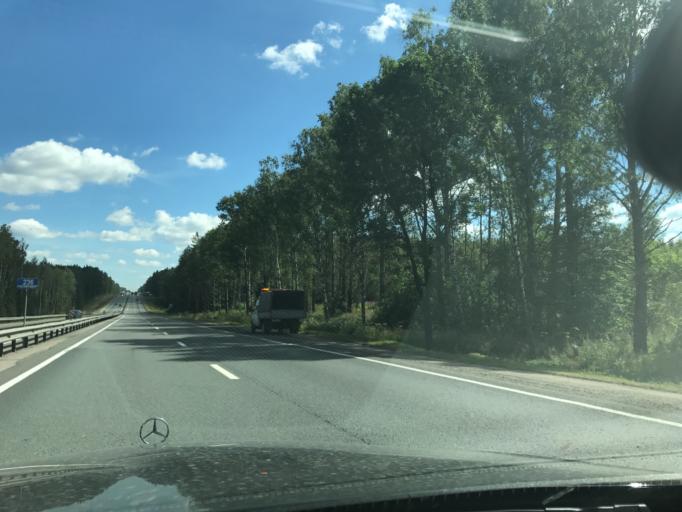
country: RU
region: Vladimir
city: Melekhovo
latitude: 56.2049
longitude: 41.1688
